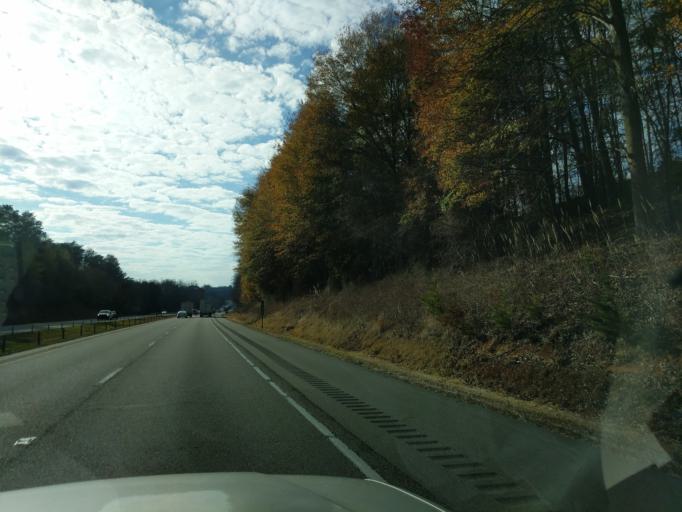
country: US
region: North Carolina
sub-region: Catawba County
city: Claremont
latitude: 35.7472
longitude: -81.0635
